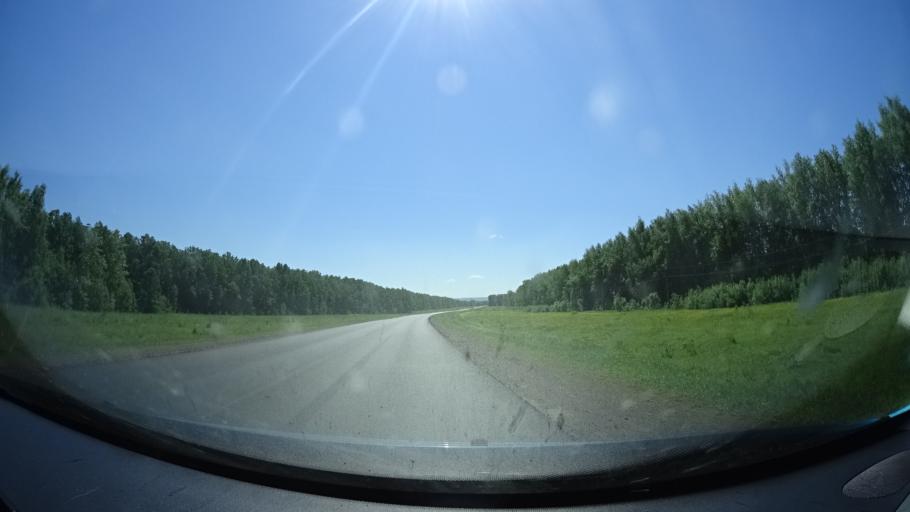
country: RU
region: Bashkortostan
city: Birsk
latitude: 55.2777
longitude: 55.7156
